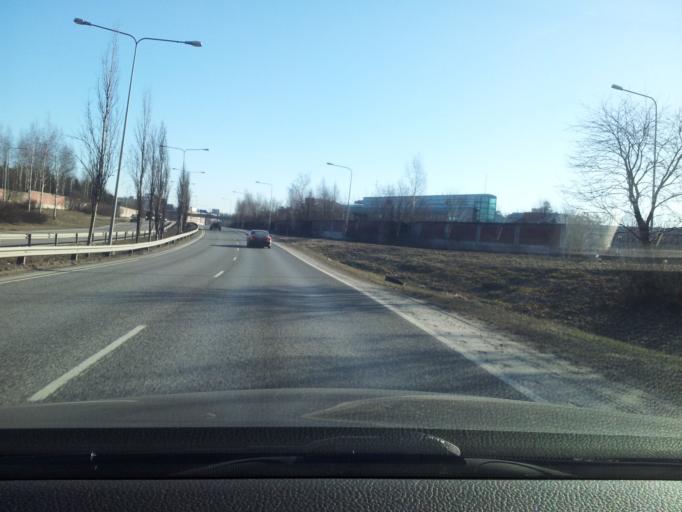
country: FI
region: Uusimaa
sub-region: Helsinki
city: Vantaa
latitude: 60.2415
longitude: 24.9832
